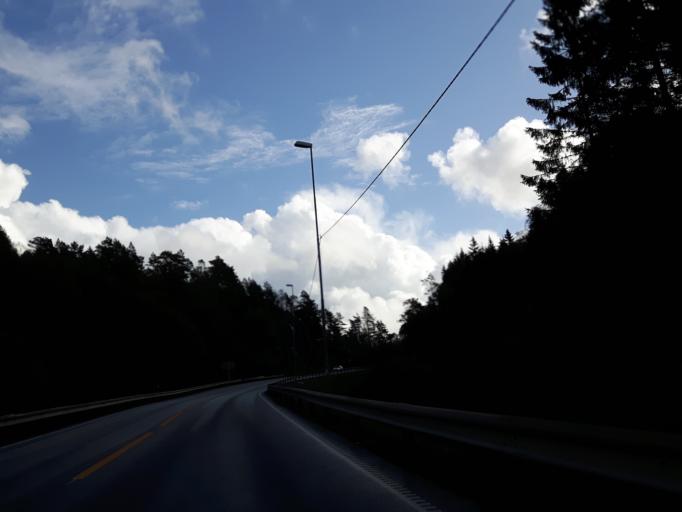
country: NO
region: Vest-Agder
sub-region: Flekkefjord
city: Flekkefjord
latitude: 58.2706
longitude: 6.7433
